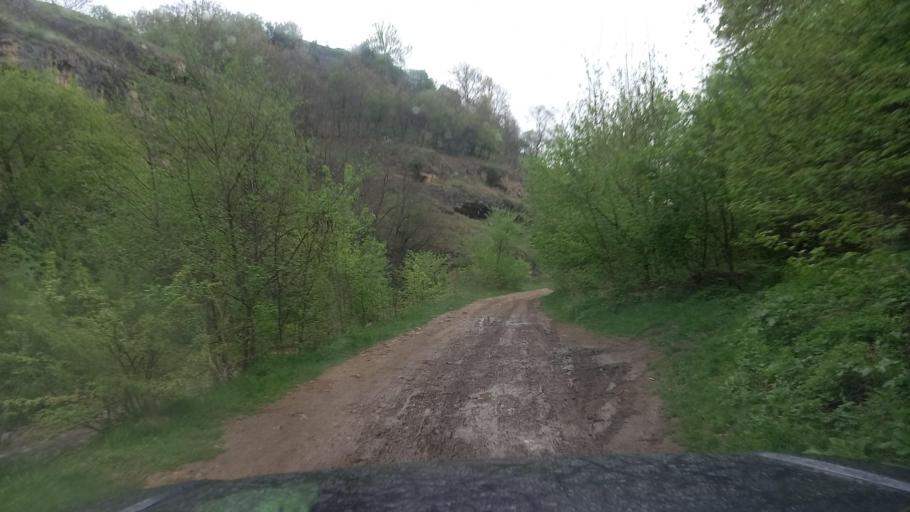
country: RU
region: Stavropol'skiy
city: Kislovodsk
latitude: 43.8877
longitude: 42.7043
